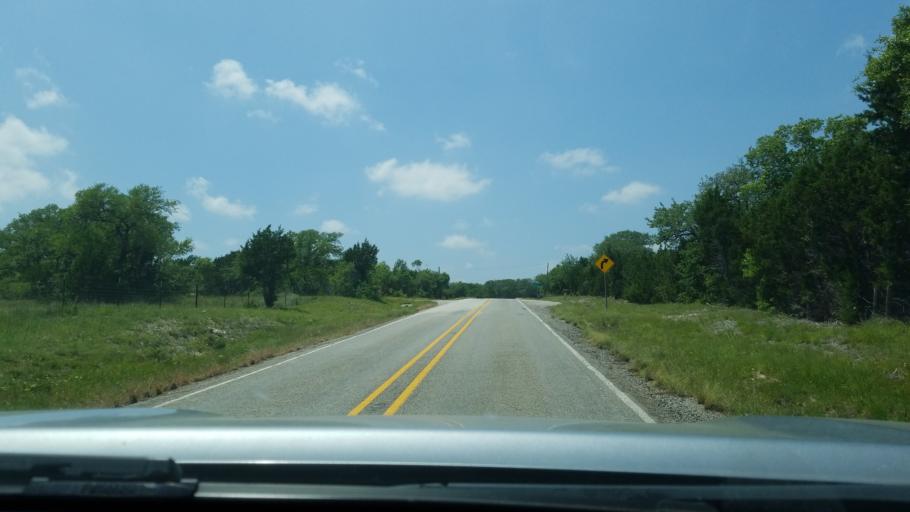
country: US
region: Texas
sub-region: Hays County
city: Woodcreek
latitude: 30.0990
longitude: -98.2555
